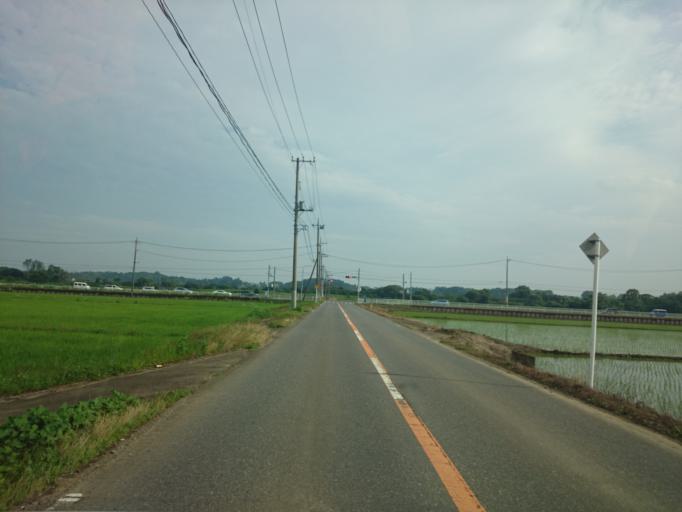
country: JP
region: Ibaraki
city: Tsukuba
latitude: 36.1461
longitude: 140.0993
